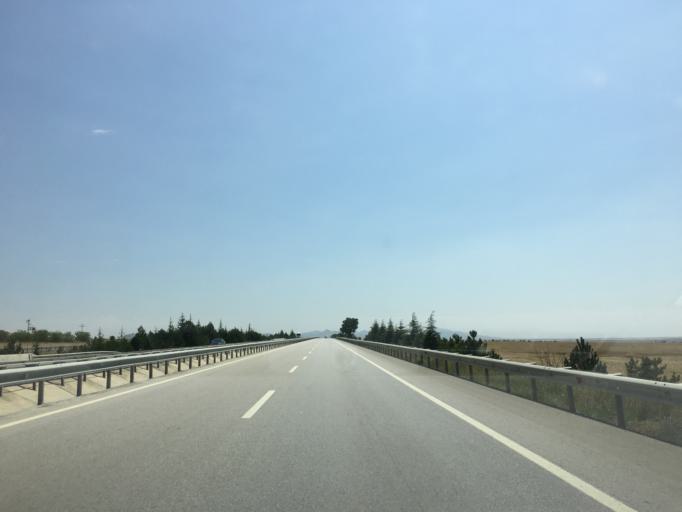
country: TR
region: Eskisehir
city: Sivrihisar
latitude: 39.4613
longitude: 31.3778
